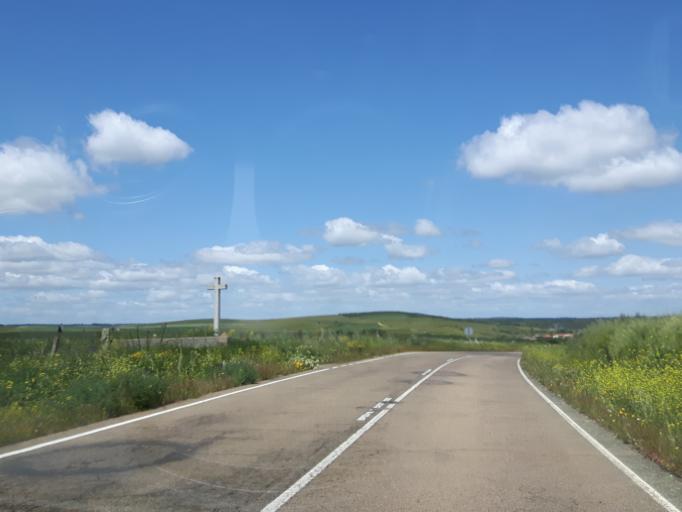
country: ES
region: Castille and Leon
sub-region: Provincia de Salamanca
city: Villar de Ciervo
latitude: 40.7319
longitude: -6.7244
